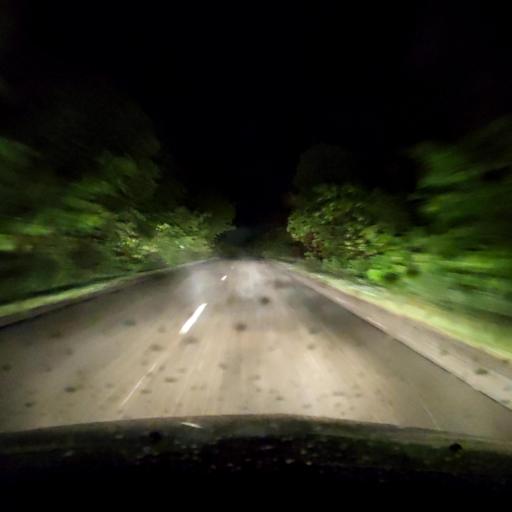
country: RU
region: Voronezj
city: Podkletnoye
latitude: 51.6258
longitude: 39.5349
